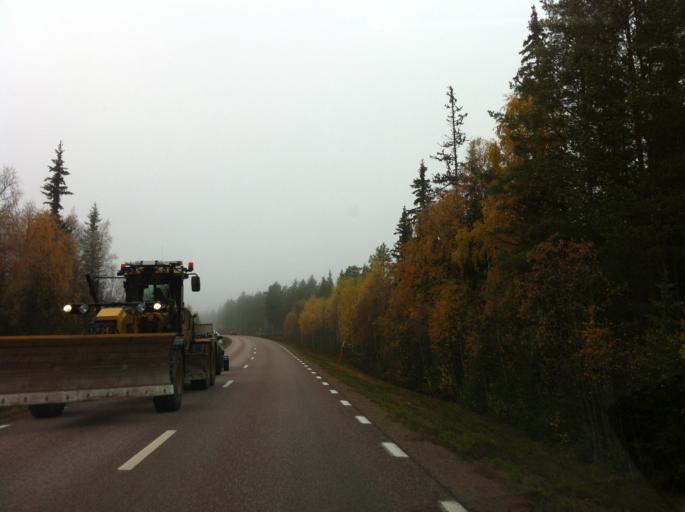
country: NO
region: Hedmark
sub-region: Trysil
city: Innbygda
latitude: 61.6944
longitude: 13.0859
